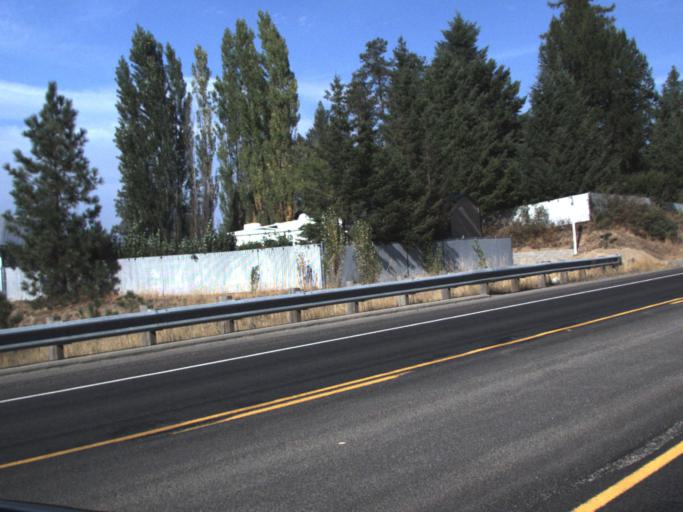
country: US
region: Washington
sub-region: Pend Oreille County
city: Newport
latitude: 48.1234
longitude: -117.1952
